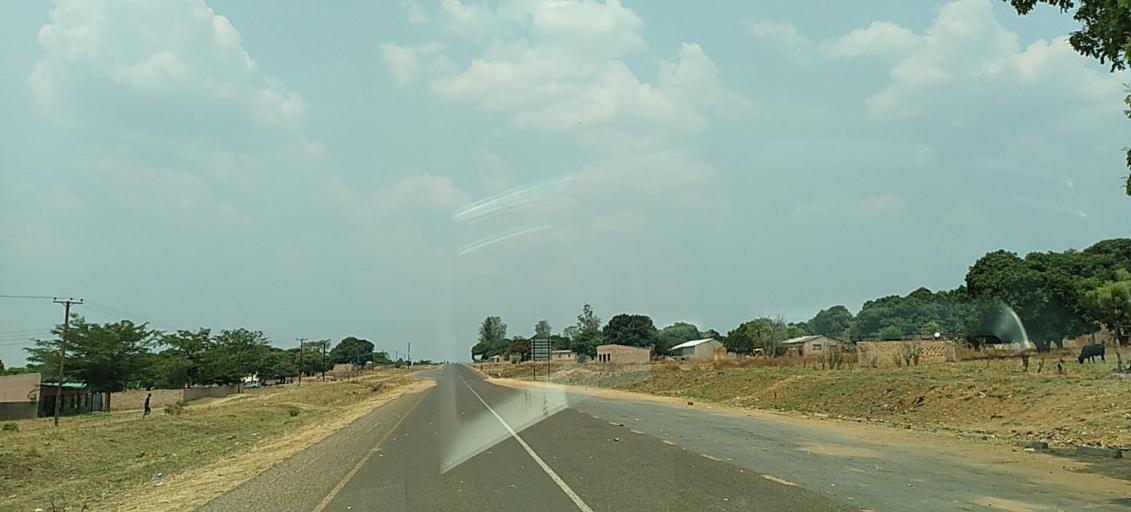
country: ZM
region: North-Western
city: Zambezi
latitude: -13.5507
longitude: 23.1124
